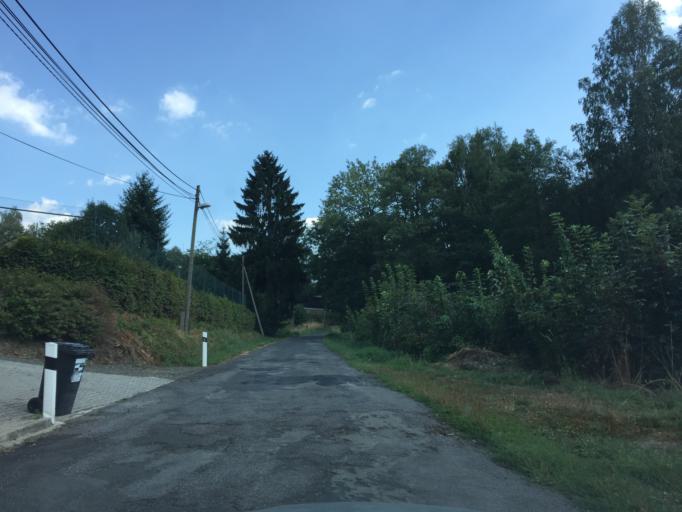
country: CZ
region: Liberecky
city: Mala Skala
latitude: 50.6708
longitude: 15.1743
